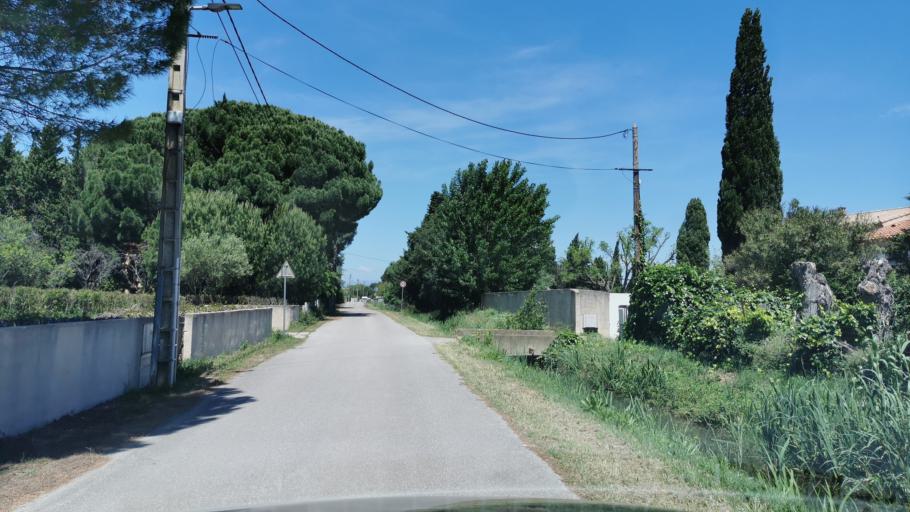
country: FR
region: Languedoc-Roussillon
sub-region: Departement de l'Aude
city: Coursan
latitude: 43.2666
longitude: 3.0231
